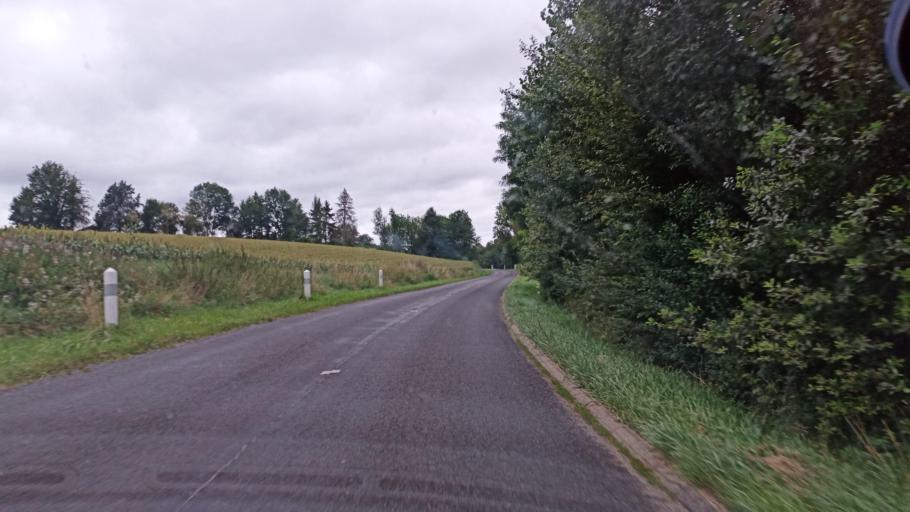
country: FR
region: Ile-de-France
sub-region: Departement de Seine-et-Marne
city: Voulx
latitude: 48.2614
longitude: 3.0122
